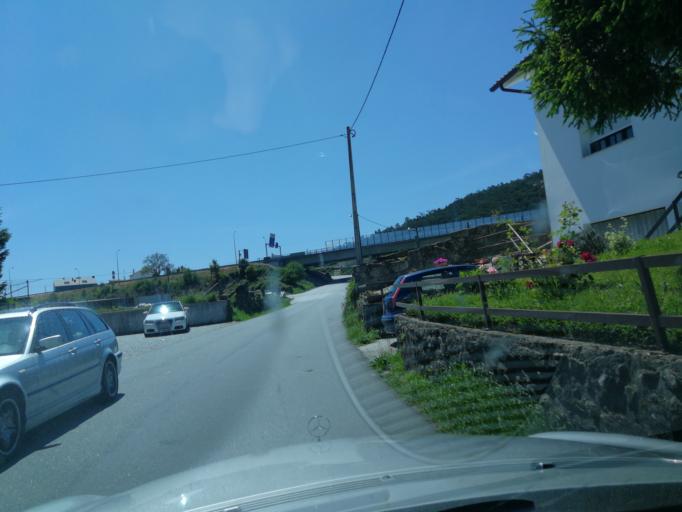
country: PT
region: Viana do Castelo
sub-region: Viana do Castelo
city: Meadela
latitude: 41.7202
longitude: -8.7966
